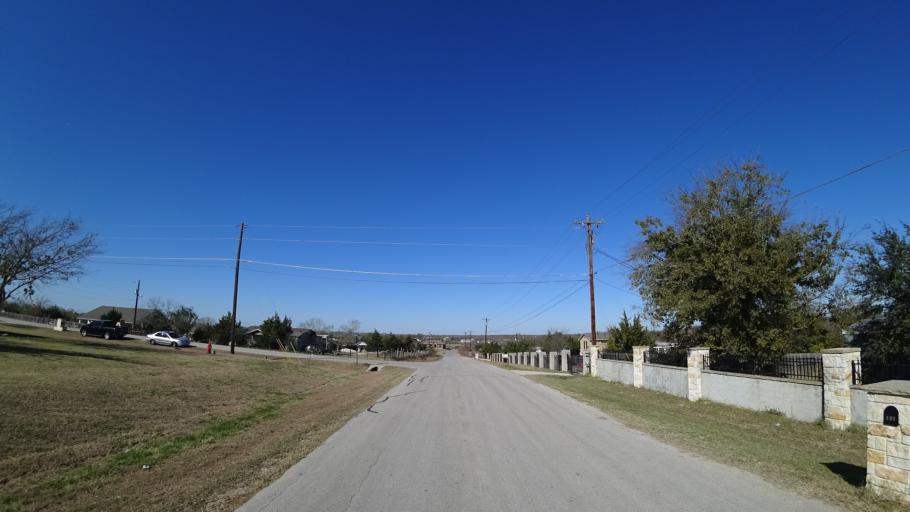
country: US
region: Texas
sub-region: Travis County
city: Garfield
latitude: 30.1025
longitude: -97.5992
